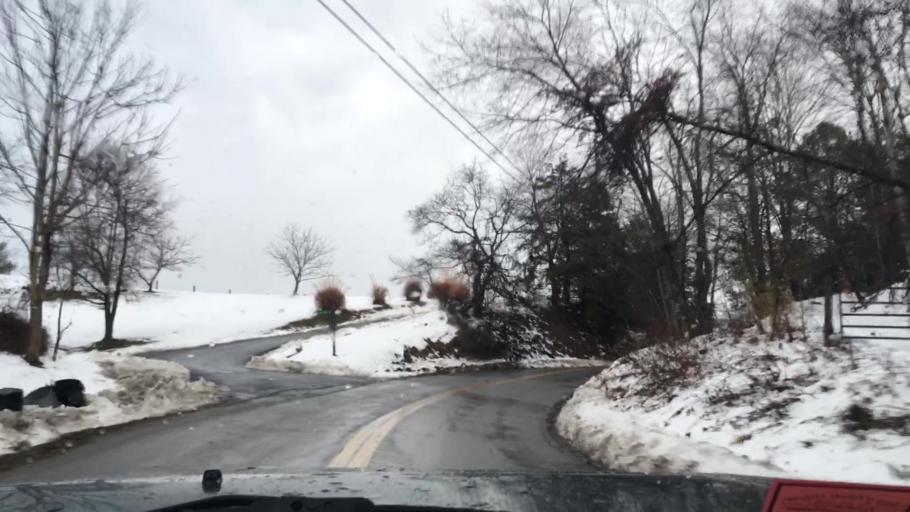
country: US
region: Virginia
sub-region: Pulaski County
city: Dublin
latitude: 37.0045
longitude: -80.6685
